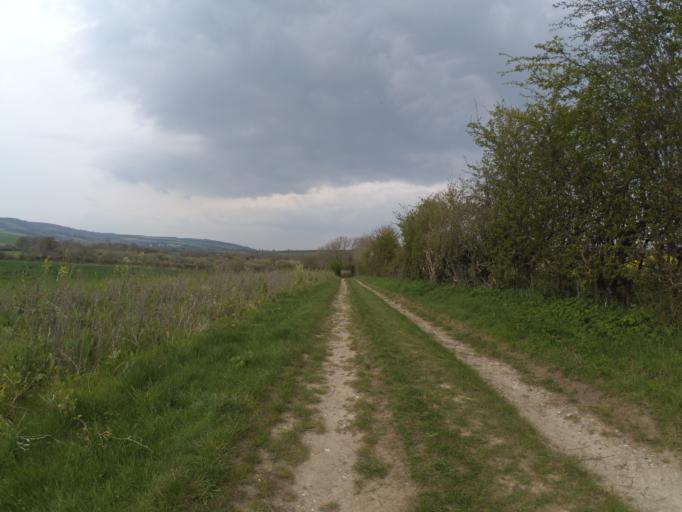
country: GB
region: England
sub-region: West Sussex
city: Arundel
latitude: 50.8778
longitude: -0.5301
